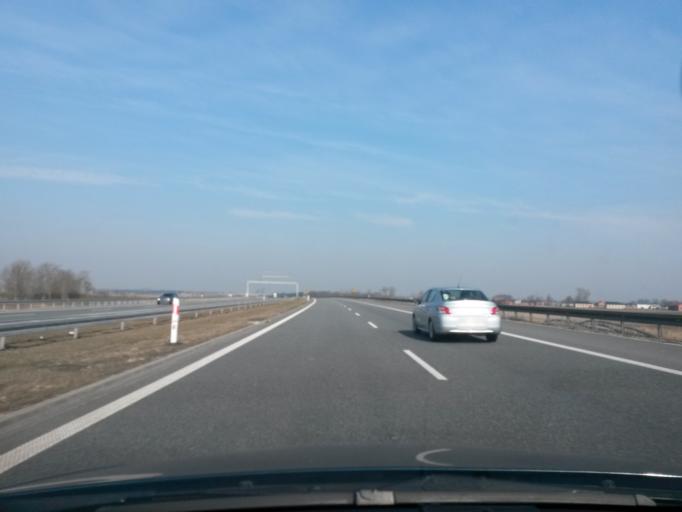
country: PL
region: Lodz Voivodeship
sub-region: Powiat leczycki
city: Piatek
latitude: 52.0743
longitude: 19.5337
